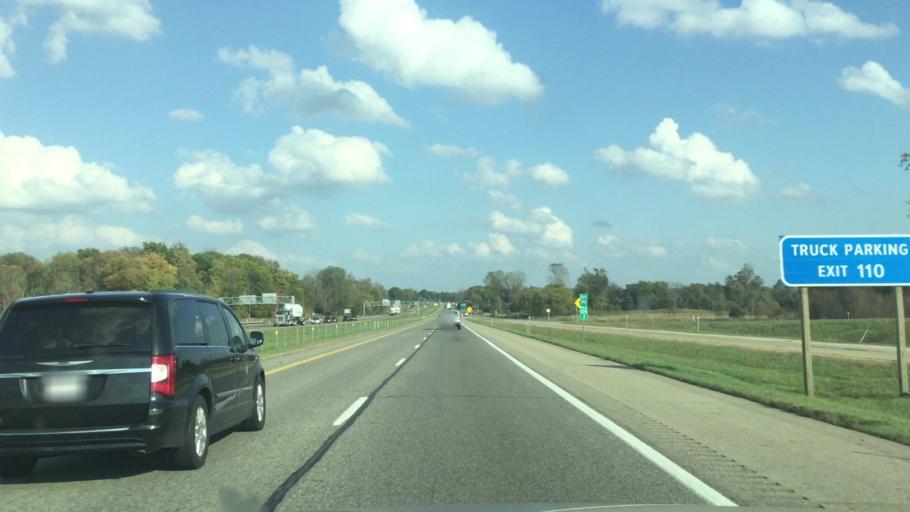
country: US
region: Michigan
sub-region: Calhoun County
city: Marshall
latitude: 42.2972
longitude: -84.9938
